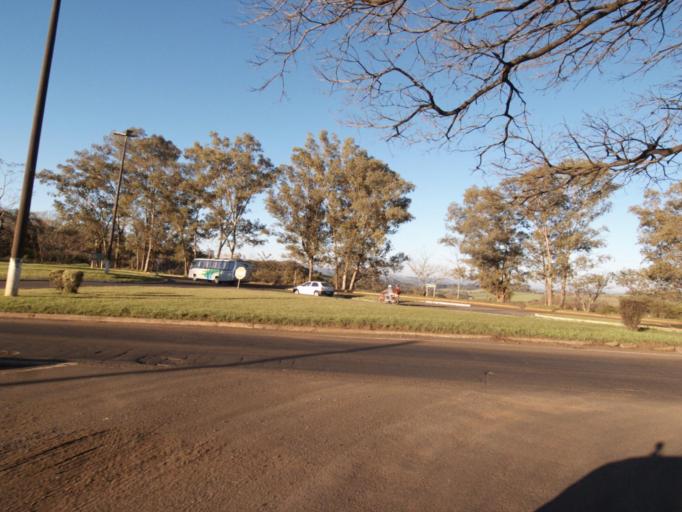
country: BR
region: Santa Catarina
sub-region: Chapeco
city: Chapeco
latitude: -26.8530
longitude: -52.9804
